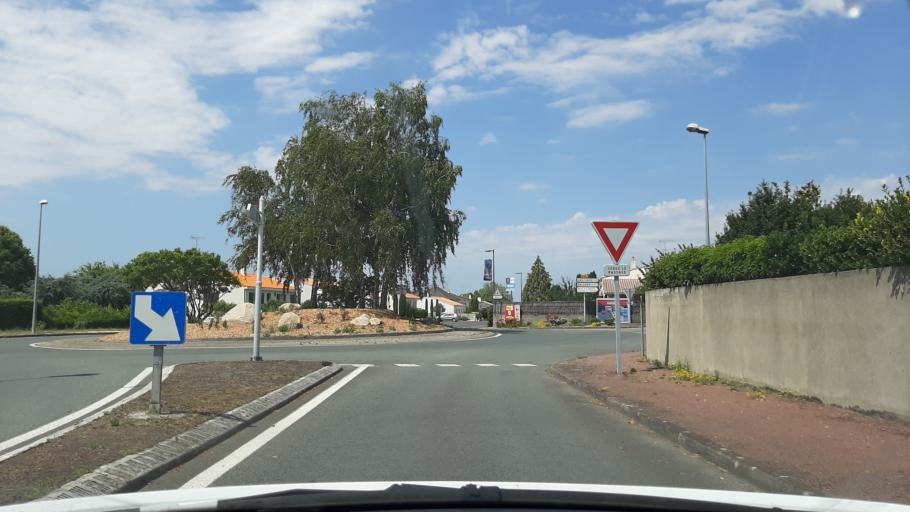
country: FR
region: Pays de la Loire
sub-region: Departement de la Vendee
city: Le Poire-sur-Vie
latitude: 46.7660
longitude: -1.4978
